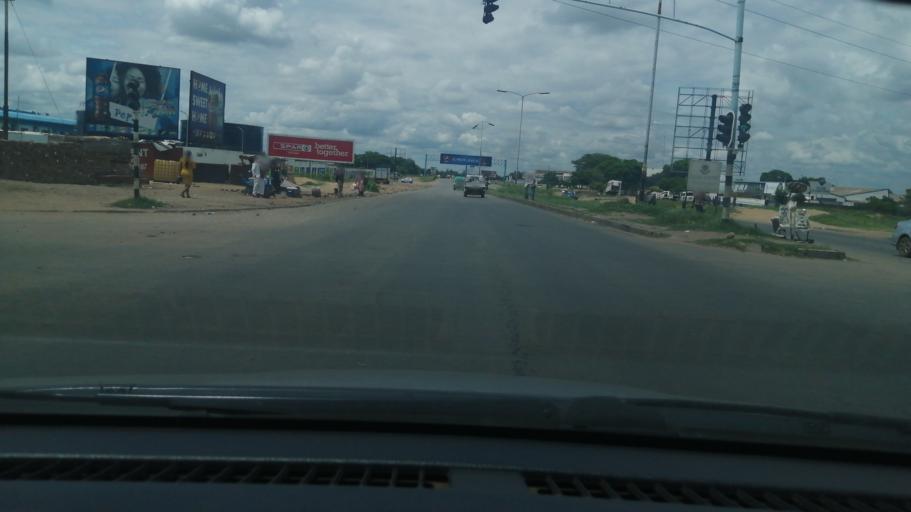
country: ZW
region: Harare
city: Harare
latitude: -17.8735
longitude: 31.0194
